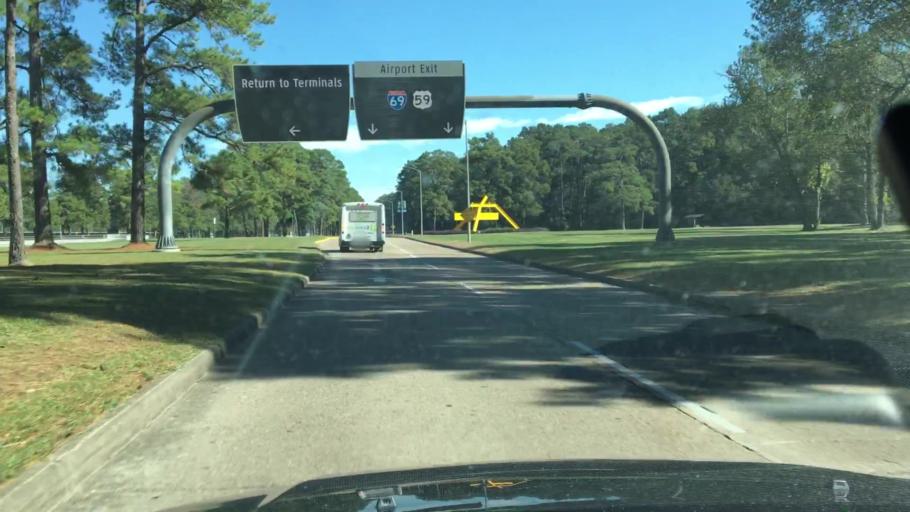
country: US
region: Texas
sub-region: Harris County
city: Humble
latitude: 29.9848
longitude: -95.3199
